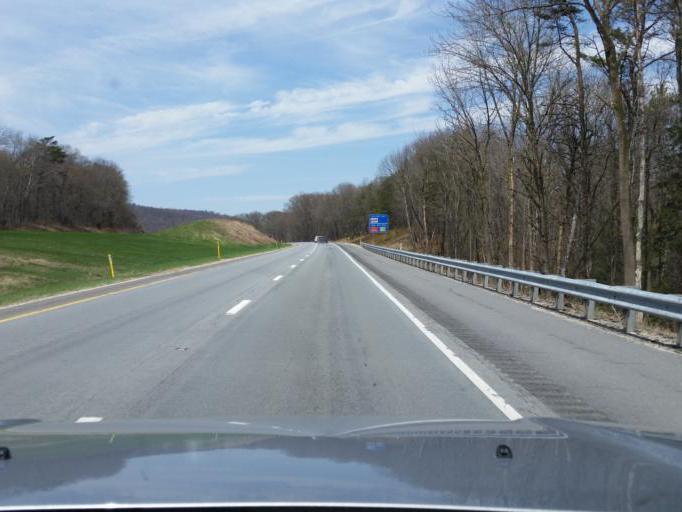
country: US
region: Pennsylvania
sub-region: Perry County
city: Newport
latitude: 40.4886
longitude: -77.0761
